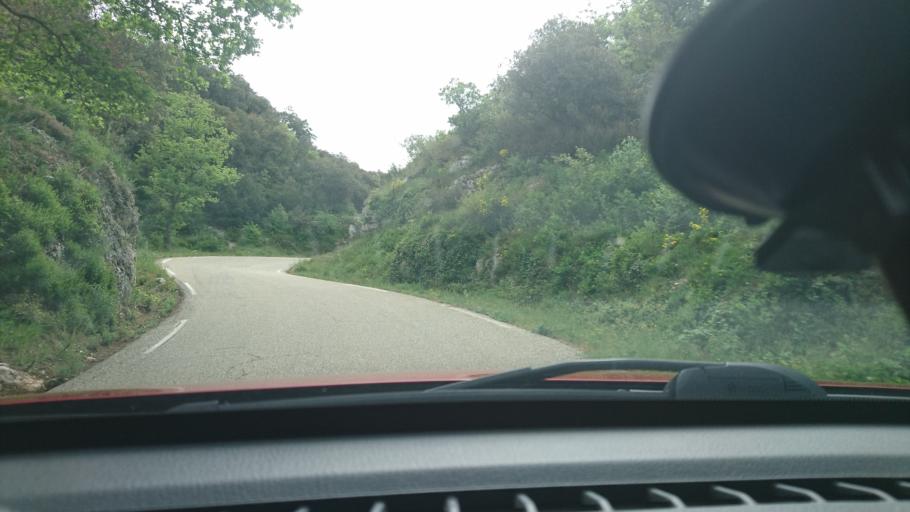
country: FR
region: Provence-Alpes-Cote d'Azur
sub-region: Departement du Vaucluse
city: Venasque
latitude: 43.9857
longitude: 5.1972
